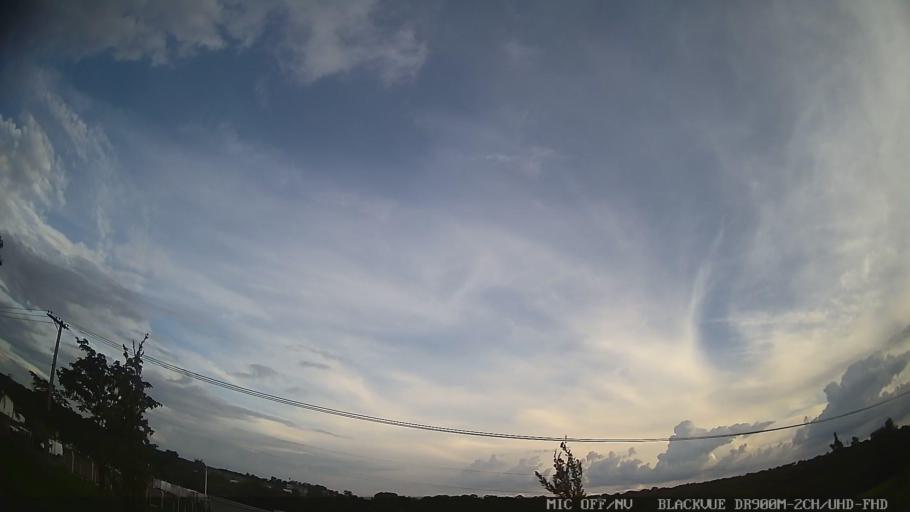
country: BR
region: Sao Paulo
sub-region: Jaguariuna
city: Jaguariuna
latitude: -22.6314
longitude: -47.0348
